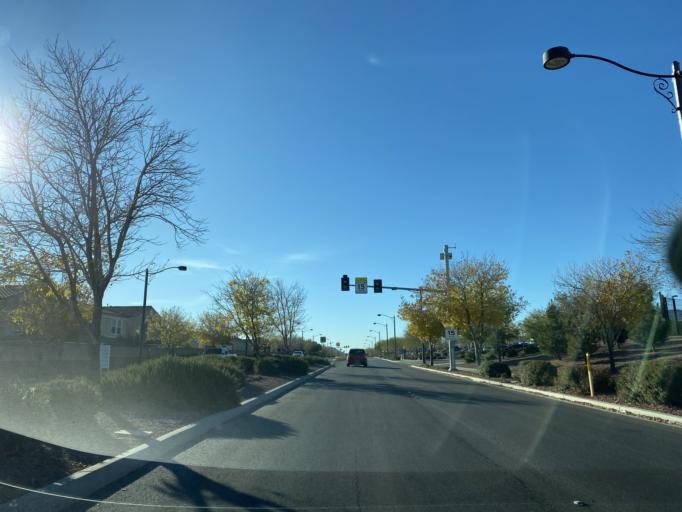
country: US
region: Nevada
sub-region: Clark County
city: Summerlin South
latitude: 36.2982
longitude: -115.3196
